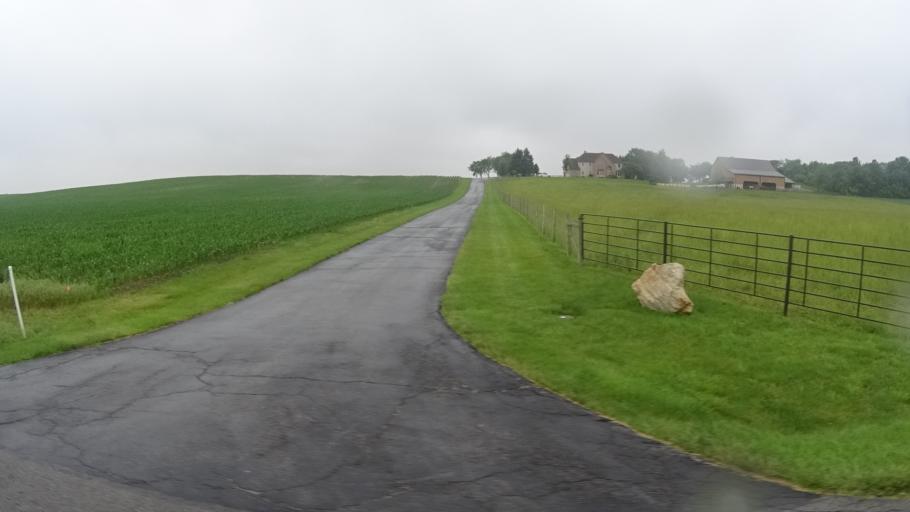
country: US
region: Ohio
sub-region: Huron County
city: Bellevue
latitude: 41.3343
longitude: -82.8434
